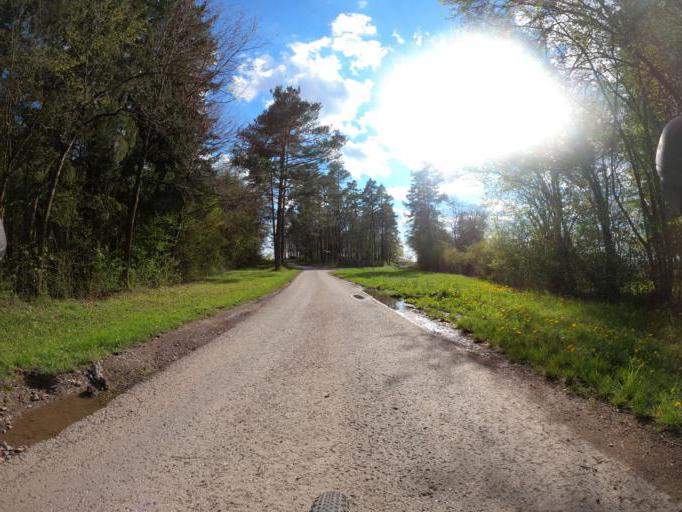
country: DE
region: Baden-Wuerttemberg
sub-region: Karlsruhe Region
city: Ostelsheim
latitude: 48.7203
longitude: 8.8366
